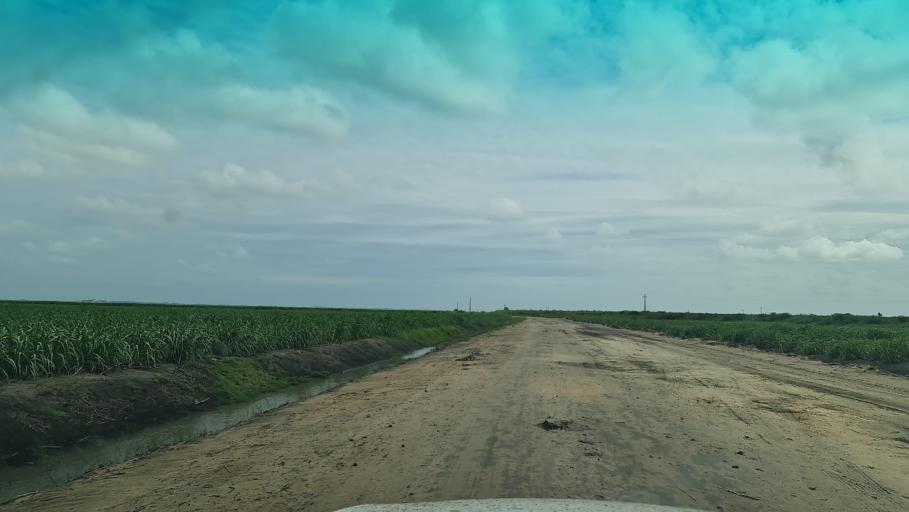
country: MZ
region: Maputo
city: Manhica
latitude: -25.4583
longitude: 32.8187
